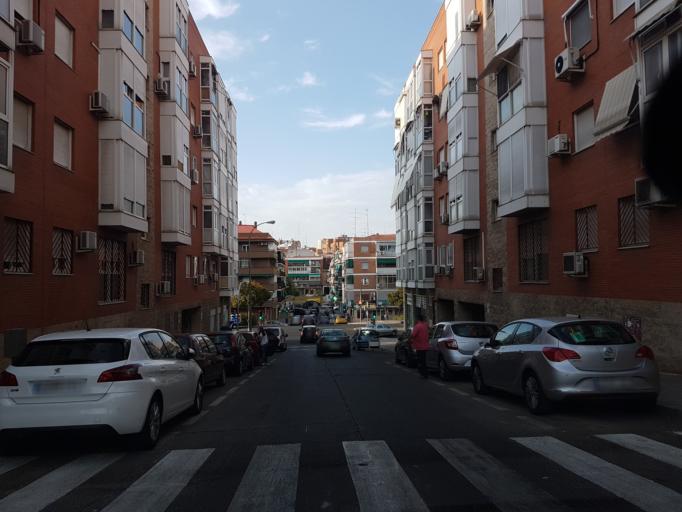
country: ES
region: Madrid
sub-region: Provincia de Madrid
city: Moratalaz
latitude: 40.4284
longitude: -3.6466
